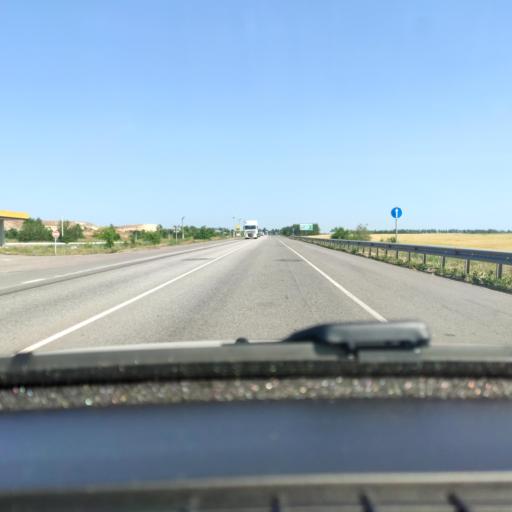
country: RU
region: Voronezj
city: Novaya Usman'
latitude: 51.6880
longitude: 39.4695
